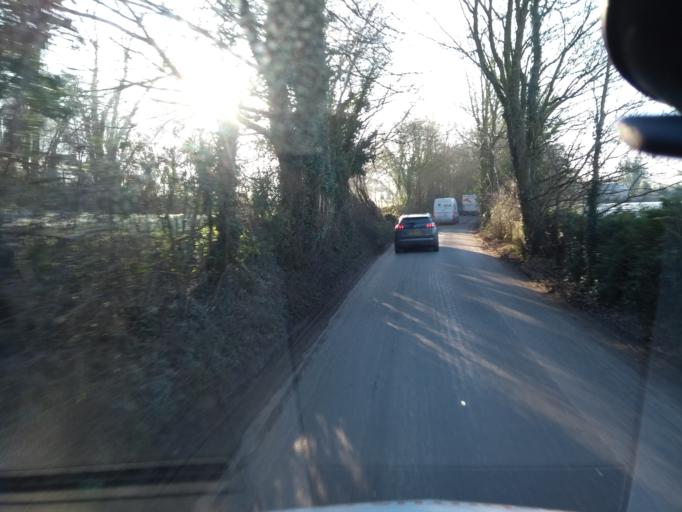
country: GB
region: England
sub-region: Somerset
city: Bruton
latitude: 51.1187
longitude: -2.4556
